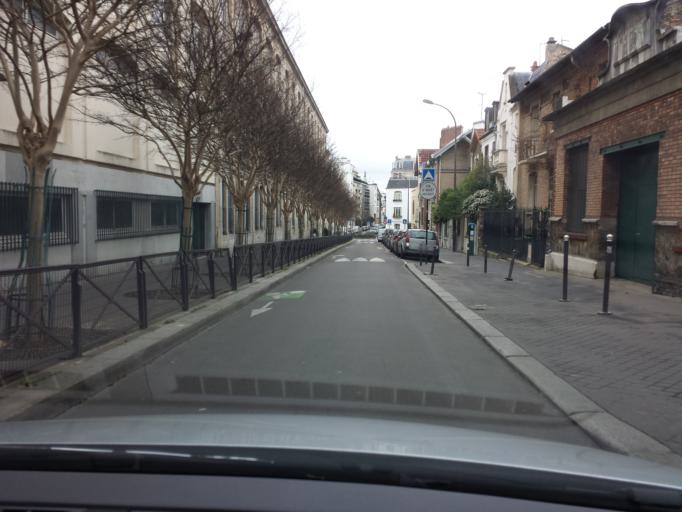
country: FR
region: Ile-de-France
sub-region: Departement du Val-de-Marne
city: Le Kremlin-Bicetre
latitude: 48.8258
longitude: 2.3552
